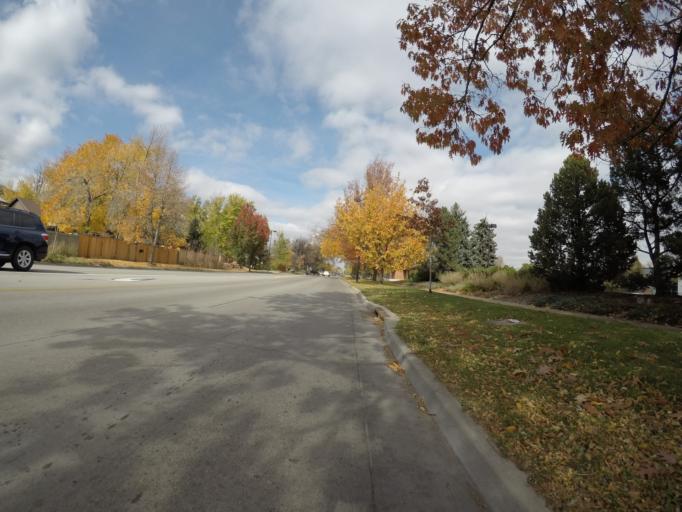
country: US
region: Colorado
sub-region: Boulder County
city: Boulder
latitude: 40.0322
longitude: -105.2820
